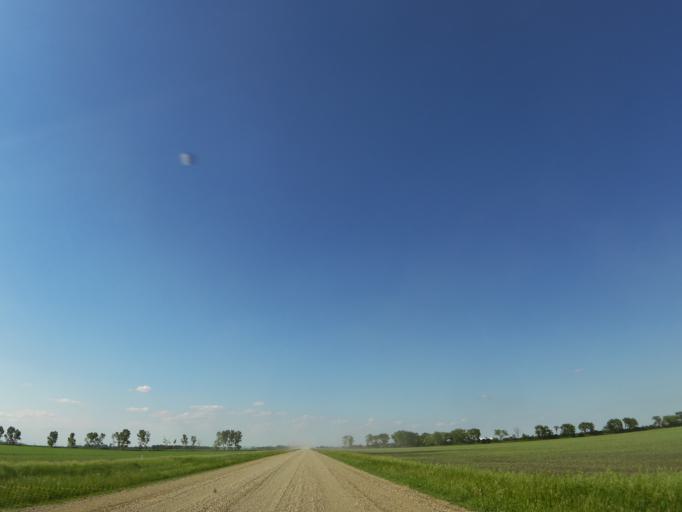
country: US
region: North Dakota
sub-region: Walsh County
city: Grafton
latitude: 48.3273
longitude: -97.2554
